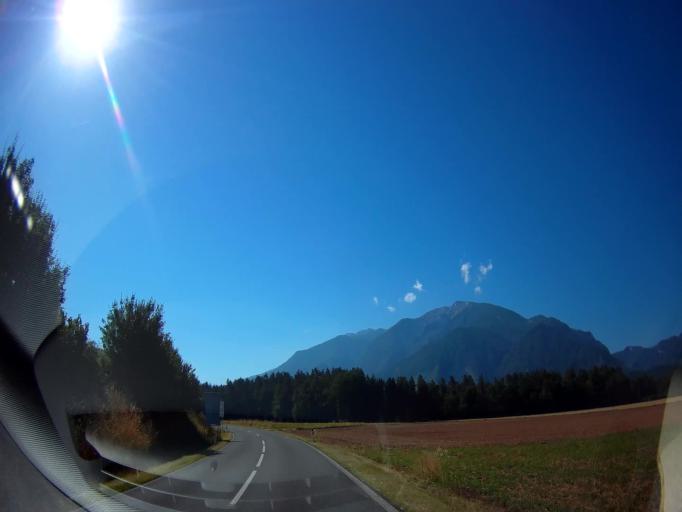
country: AT
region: Carinthia
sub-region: Politischer Bezirk Volkermarkt
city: Globasnitz
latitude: 46.5765
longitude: 14.7318
